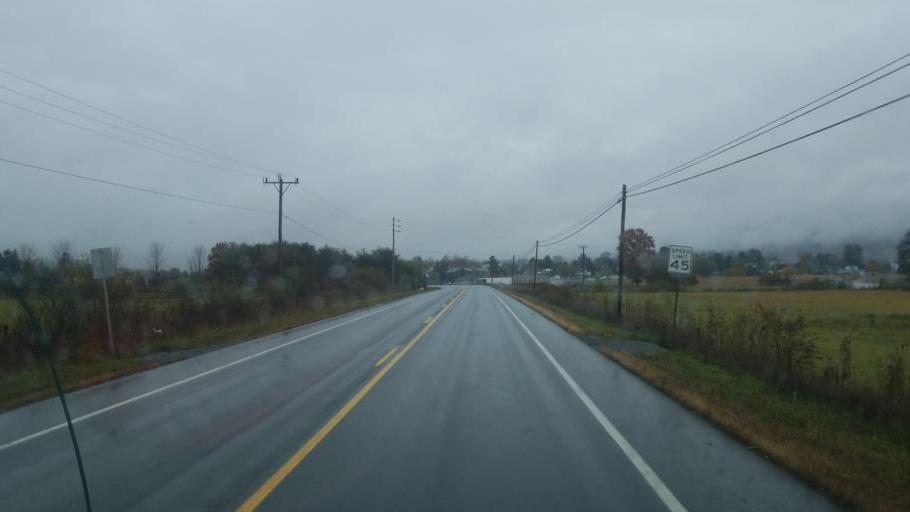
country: US
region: Pennsylvania
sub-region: Clinton County
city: Mill Hall
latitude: 41.0631
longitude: -77.6081
